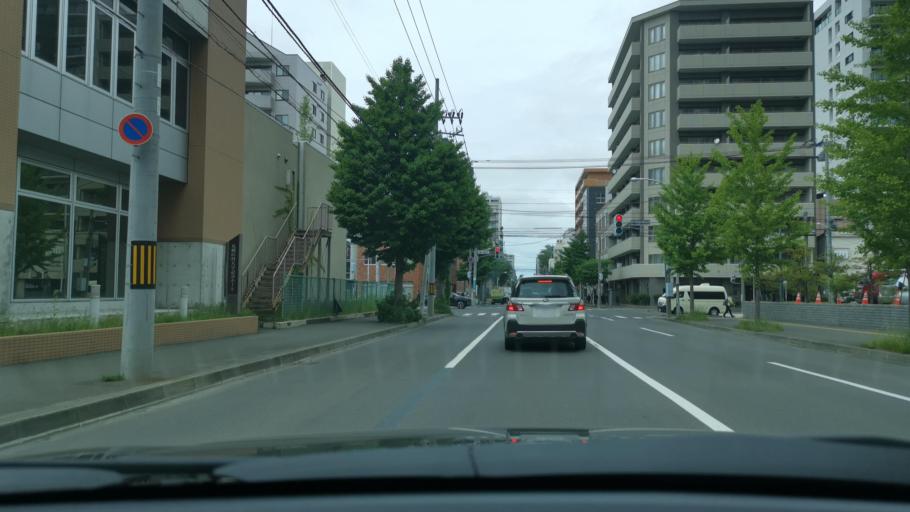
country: JP
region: Hokkaido
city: Sapporo
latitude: 43.0556
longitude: 141.3307
